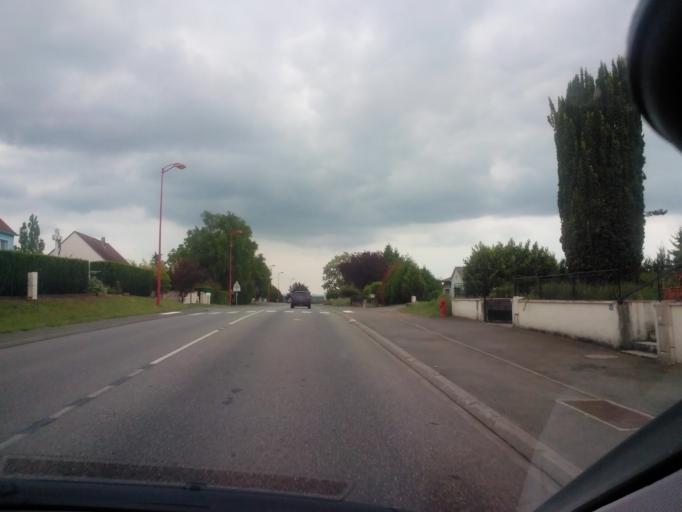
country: FR
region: Lorraine
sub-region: Departement de la Moselle
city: Willerwald
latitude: 49.0221
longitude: 7.0380
